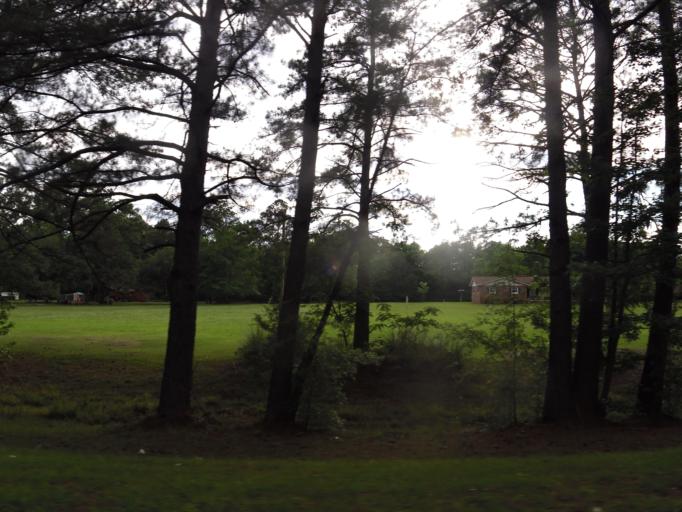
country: US
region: South Carolina
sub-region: Jasper County
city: Hardeeville
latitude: 32.3267
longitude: -81.0900
